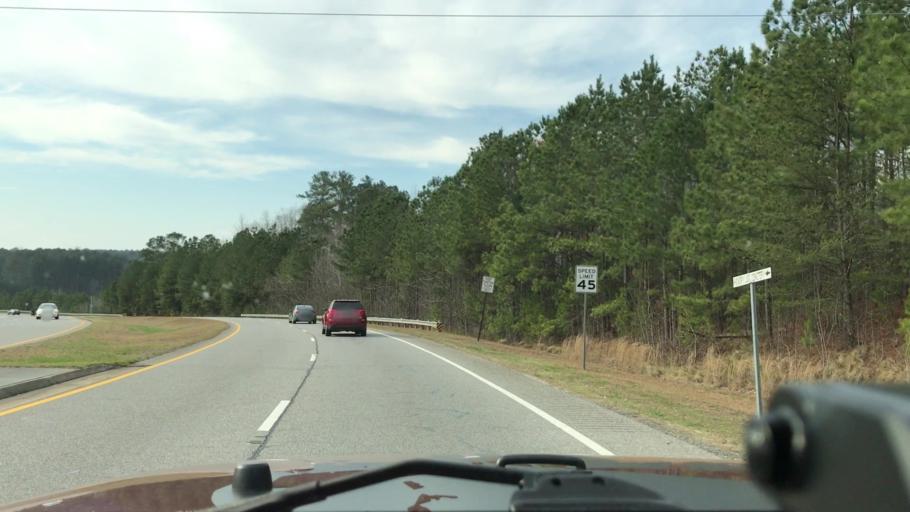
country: US
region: Georgia
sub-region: Cherokee County
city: Canton
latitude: 34.2575
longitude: -84.4821
